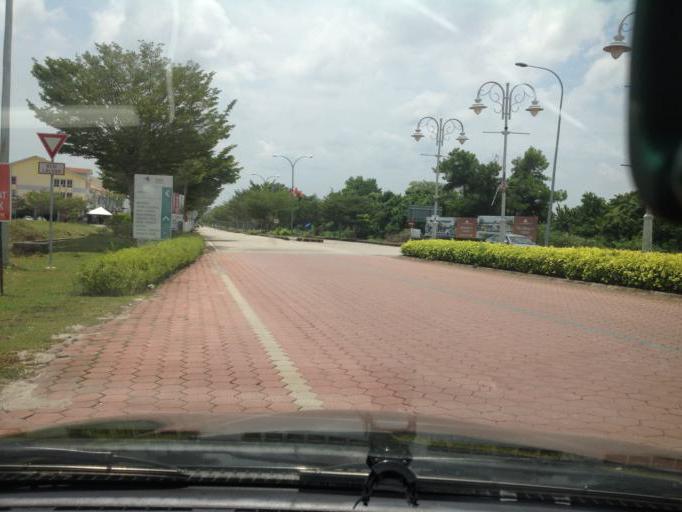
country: MY
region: Kedah
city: Sungai Petani
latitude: 5.6177
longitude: 100.5506
